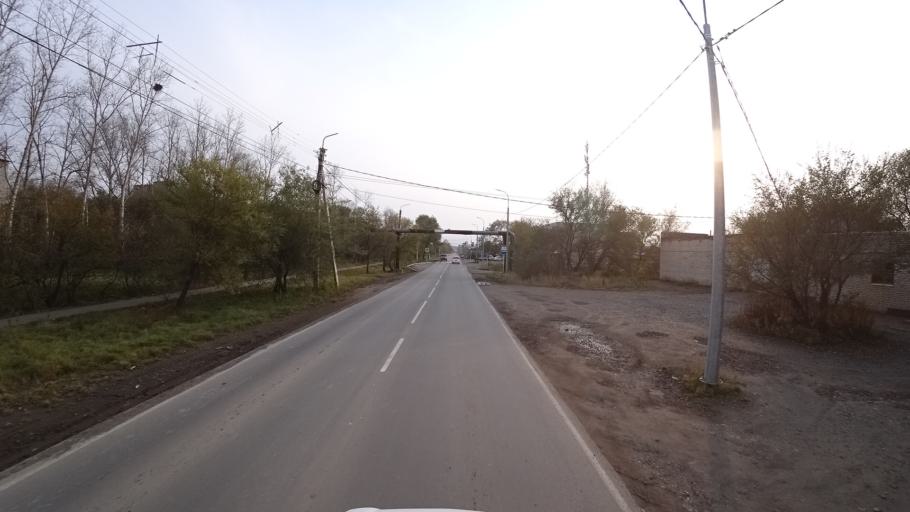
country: RU
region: Khabarovsk Krai
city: Amursk
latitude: 50.0982
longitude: 136.5079
